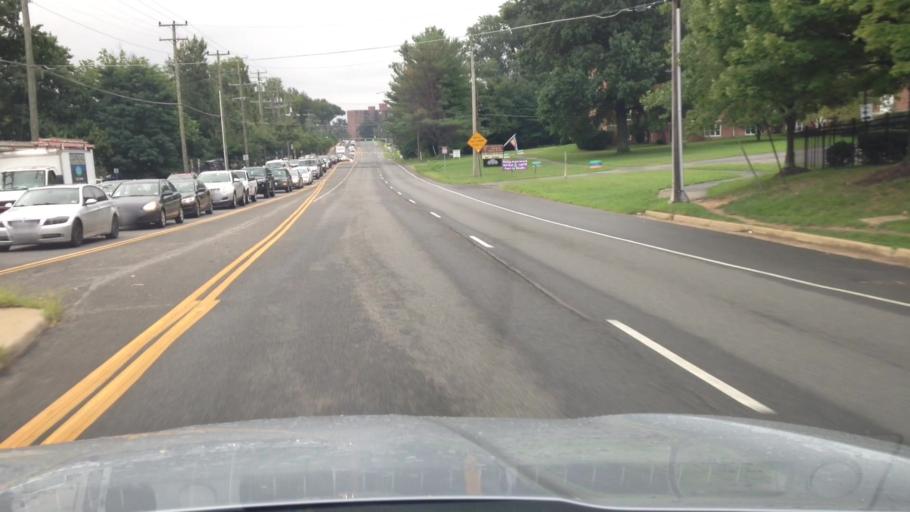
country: US
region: Virginia
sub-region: Fairfax County
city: Seven Corners
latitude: 38.8647
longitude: -77.1501
